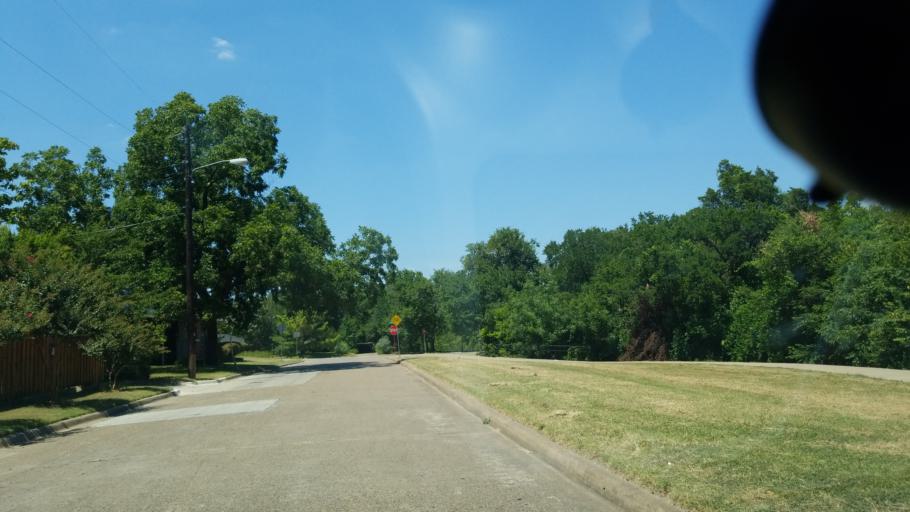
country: US
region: Texas
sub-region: Dallas County
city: Cockrell Hill
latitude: 32.7265
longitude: -96.8483
